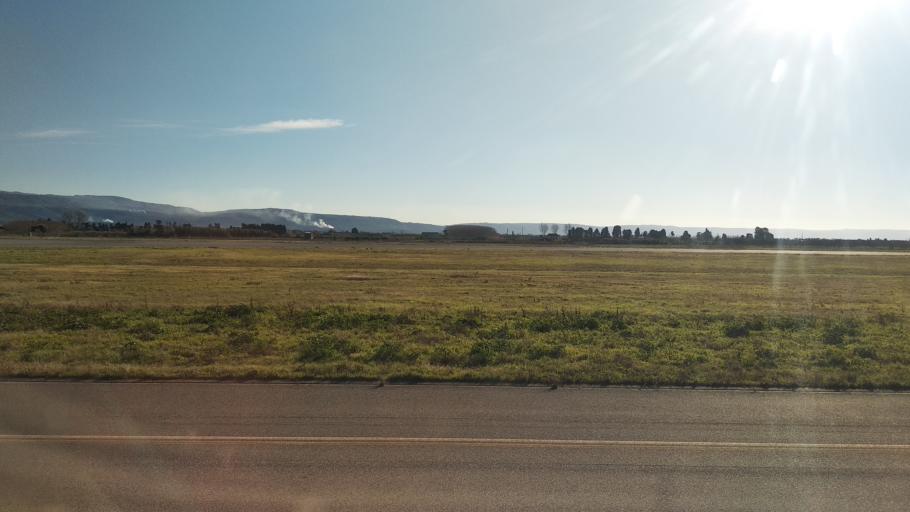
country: IT
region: Calabria
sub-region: Provincia di Catanzaro
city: Santa Eufemia Lamezia
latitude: 38.9070
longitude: 16.2480
